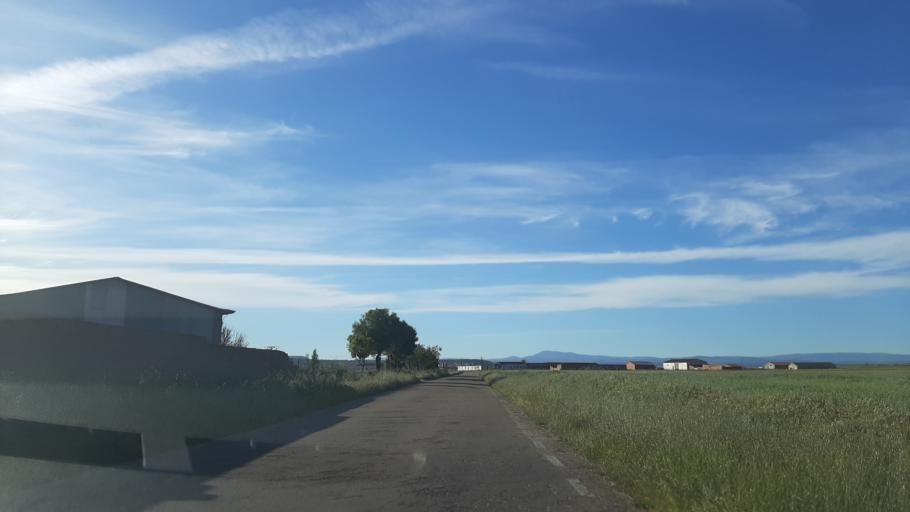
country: ES
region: Castille and Leon
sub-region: Provincia de Salamanca
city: Pedrosillo de Alba
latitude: 40.8230
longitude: -5.3992
